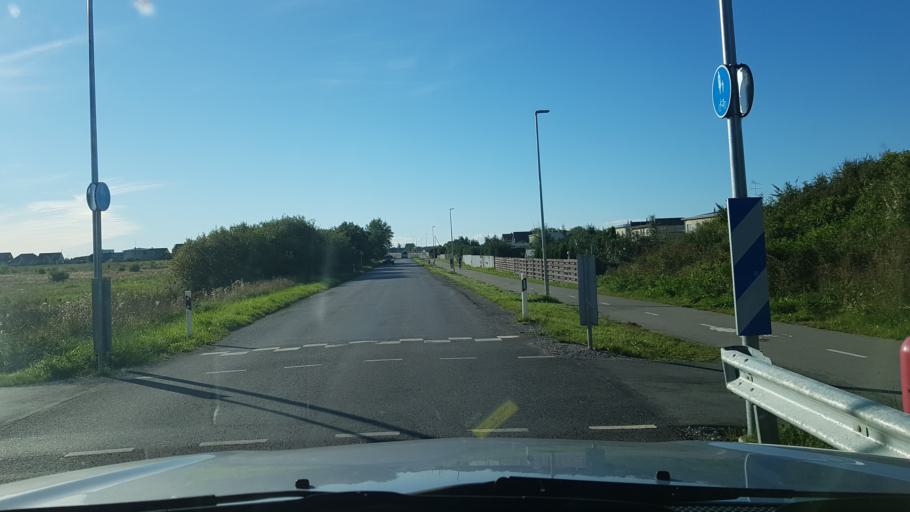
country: EE
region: Harju
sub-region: Rae vald
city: Jueri
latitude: 59.3858
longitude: 24.8573
